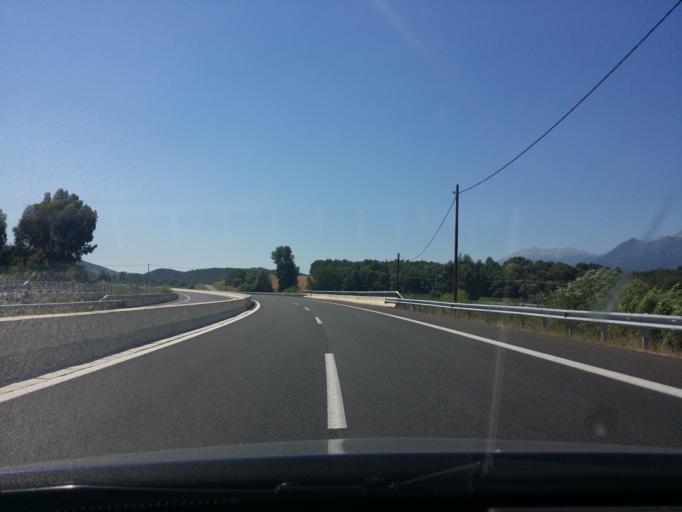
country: GR
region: Peloponnese
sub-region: Nomos Lakonias
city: Magoula
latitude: 37.1828
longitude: 22.3589
